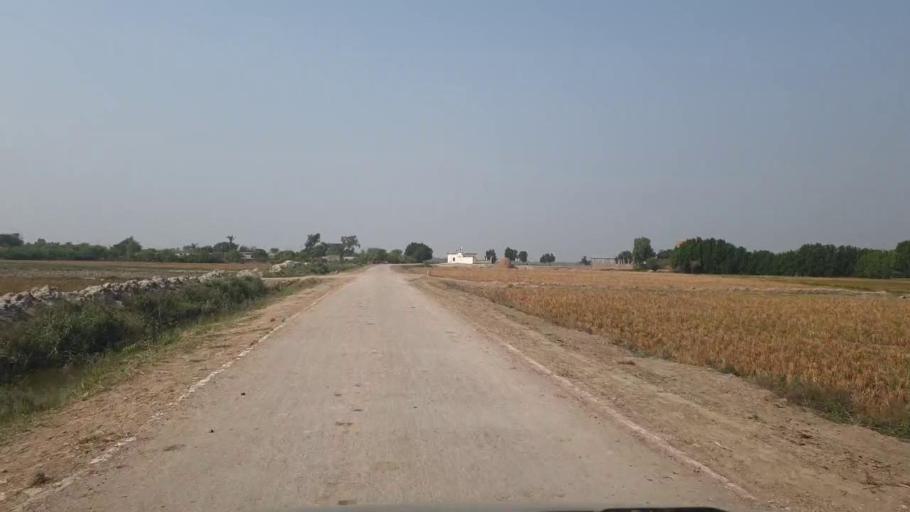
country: PK
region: Sindh
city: Bulri
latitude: 25.0327
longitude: 68.3838
